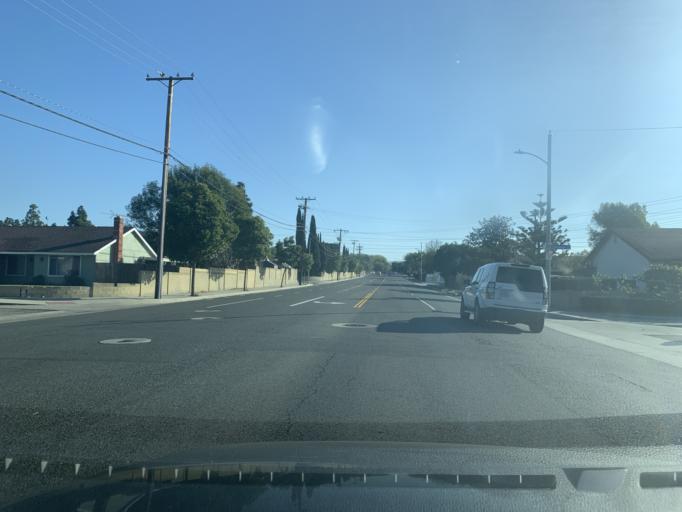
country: US
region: California
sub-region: Orange County
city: Villa Park
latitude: 33.8230
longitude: -117.8293
